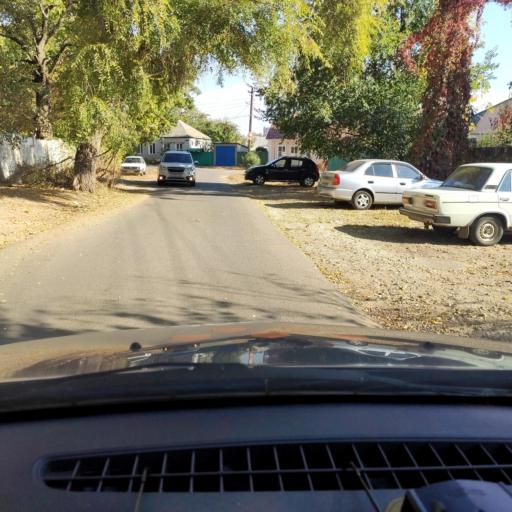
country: RU
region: Voronezj
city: Voronezh
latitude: 51.6445
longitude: 39.1705
